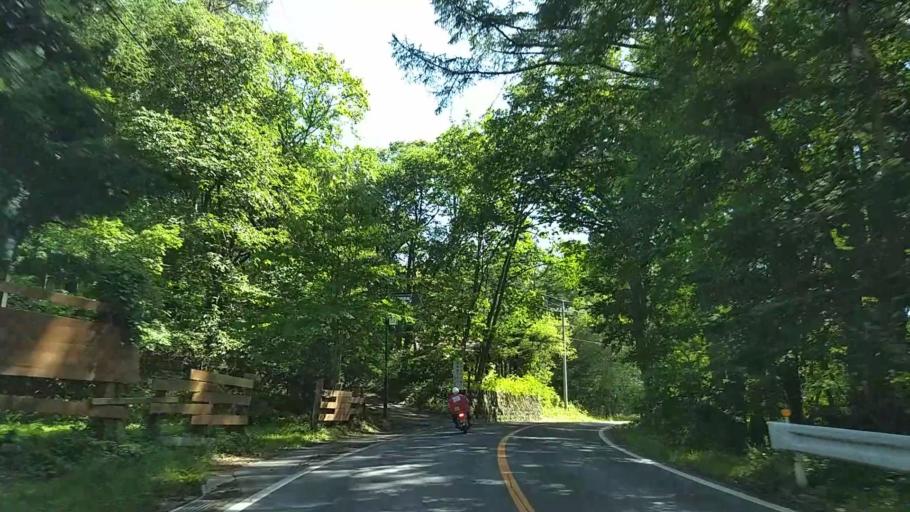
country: JP
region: Nagano
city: Chino
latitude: 36.0573
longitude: 138.2695
